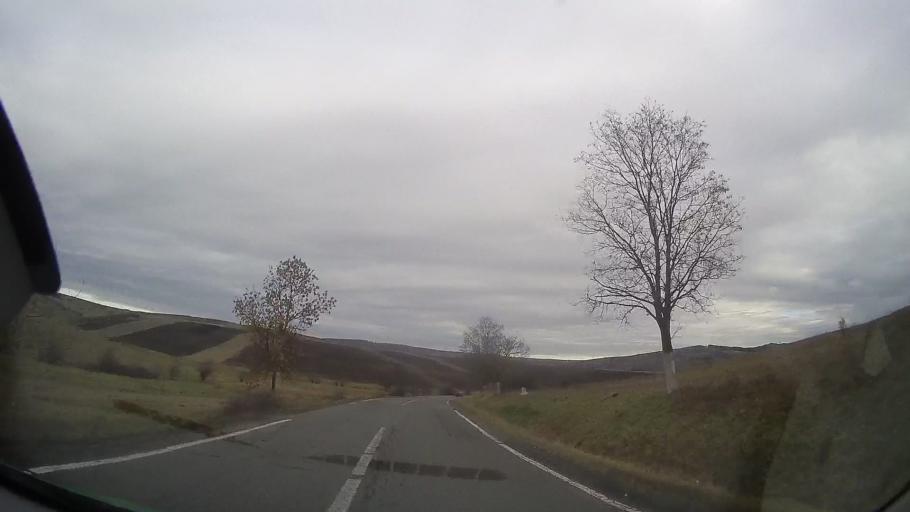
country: RO
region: Mures
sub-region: Comuna Faragau
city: Faragau
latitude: 46.7619
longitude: 24.5419
